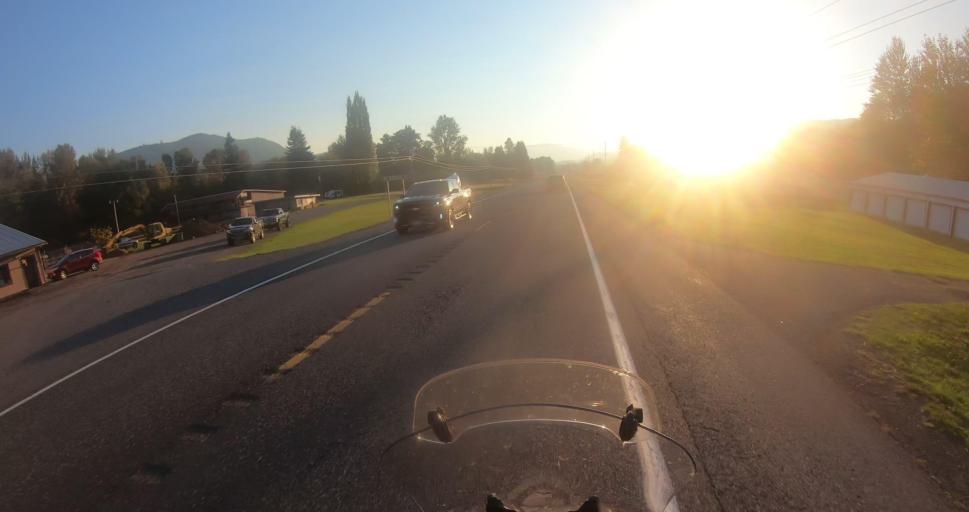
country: US
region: Washington
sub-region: Lewis County
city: Morton
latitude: 46.5315
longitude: -122.1279
